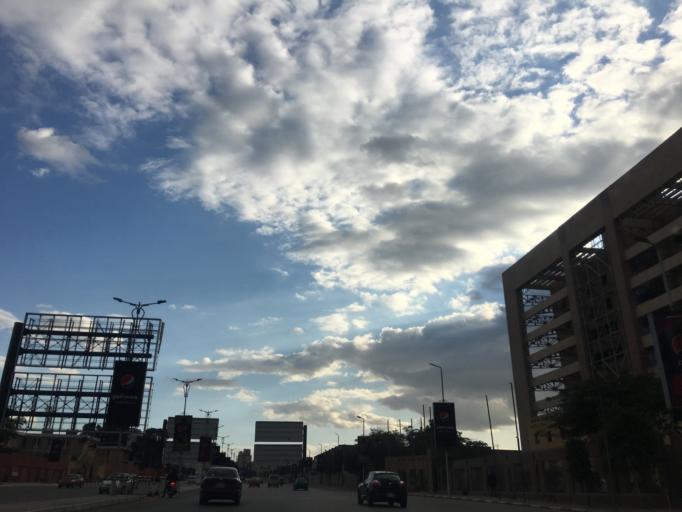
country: EG
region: Muhafazat al Qahirah
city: Cairo
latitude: 30.0506
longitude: 31.3074
